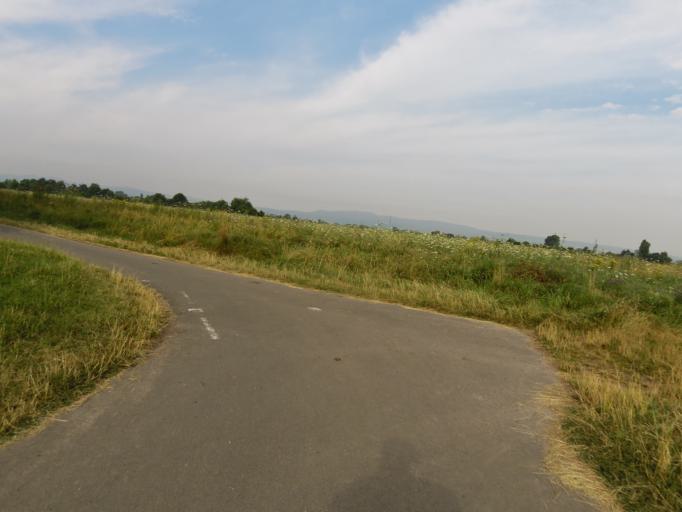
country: DE
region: Rheinland-Pfalz
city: Birkenheide
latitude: 49.4864
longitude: 8.2590
